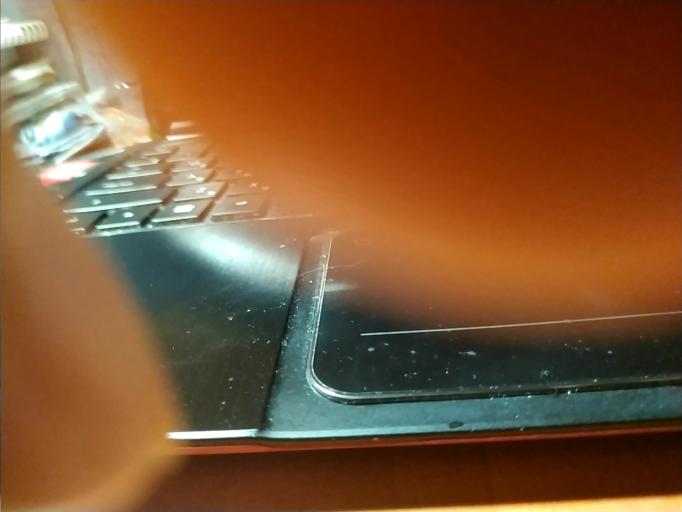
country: RU
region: Tverskaya
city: Ves'yegonsk
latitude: 58.7034
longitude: 37.5439
